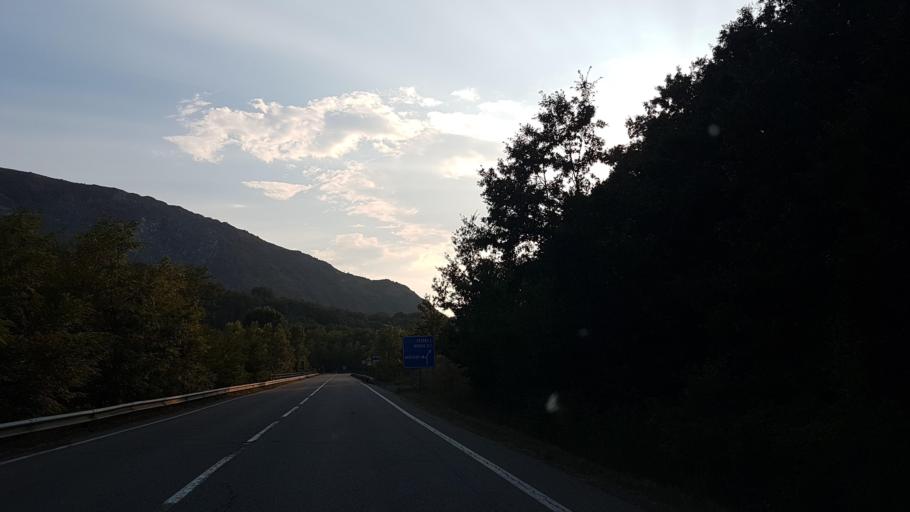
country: IT
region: Emilia-Romagna
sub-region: Provincia di Parma
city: Stazione Valmozzola
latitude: 44.5409
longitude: 9.8981
